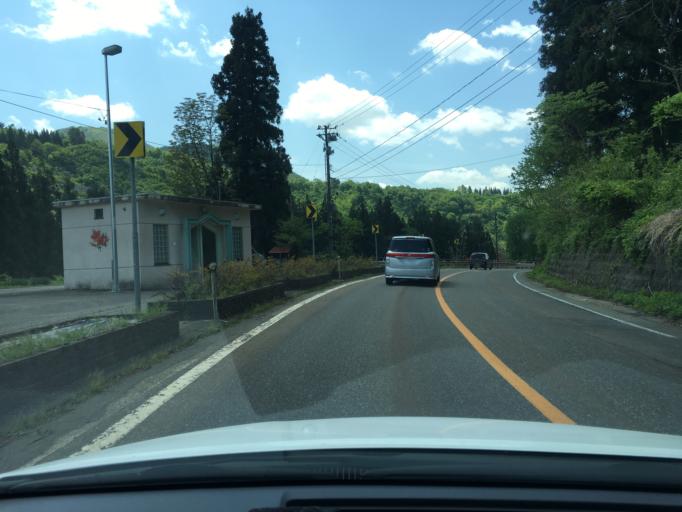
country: JP
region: Niigata
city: Tochio-honcho
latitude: 37.3078
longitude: 139.0106
